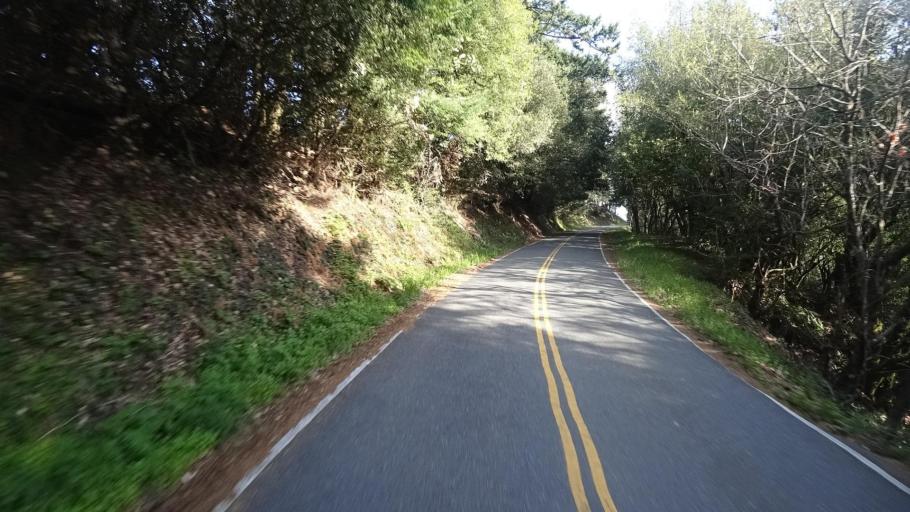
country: US
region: California
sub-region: Humboldt County
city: Blue Lake
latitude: 40.7233
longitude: -123.9444
